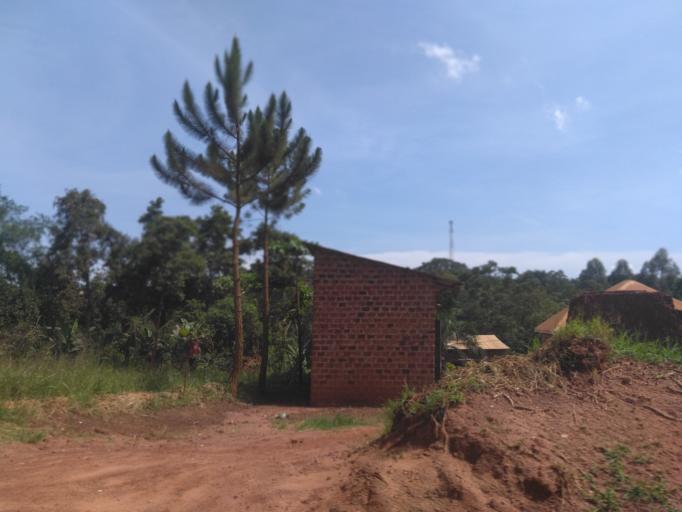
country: UG
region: Central Region
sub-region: Wakiso District
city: Kireka
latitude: 0.4455
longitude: 32.5824
